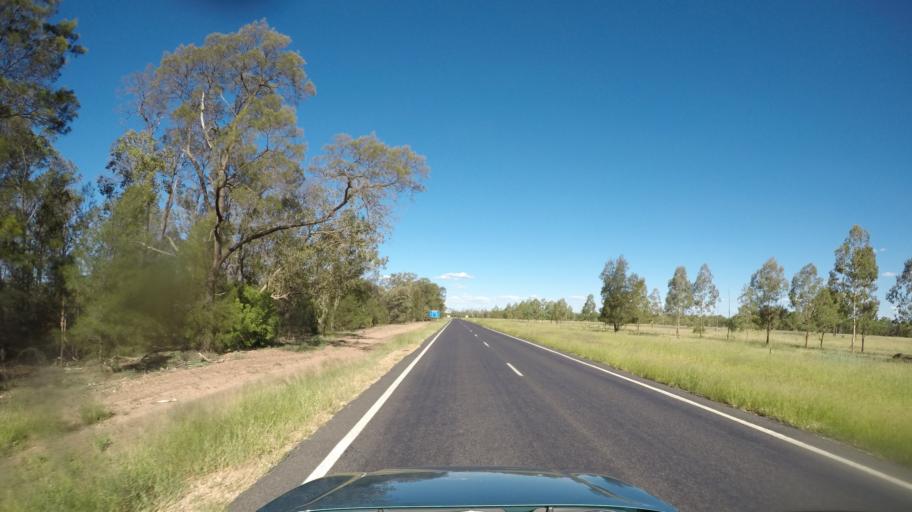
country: AU
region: Queensland
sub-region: Goondiwindi
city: Goondiwindi
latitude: -28.1605
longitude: 150.6477
